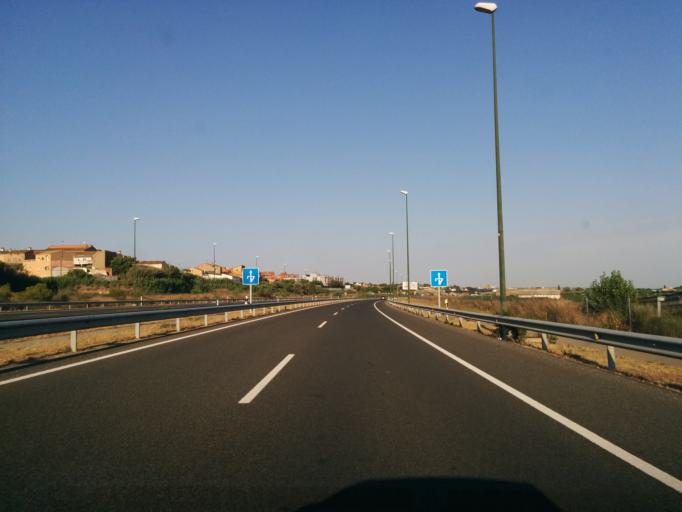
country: ES
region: Aragon
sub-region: Provincia de Zaragoza
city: Zaragoza
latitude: 41.6652
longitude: -0.8318
